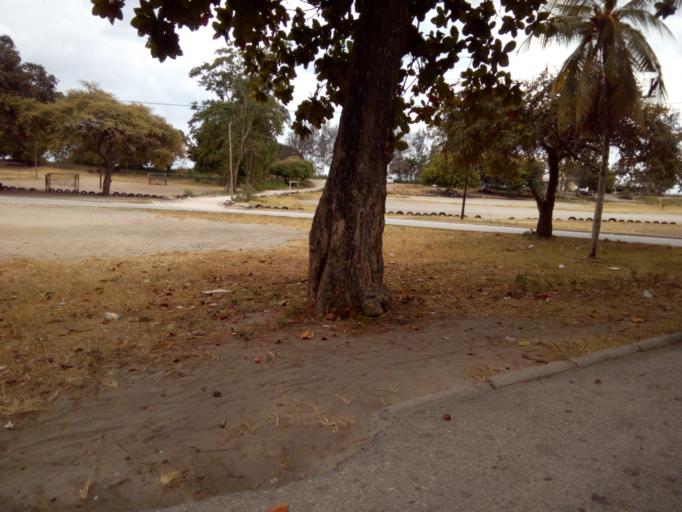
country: TZ
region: Zanzibar Urban/West
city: Zanzibar
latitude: -6.1731
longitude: 39.1961
